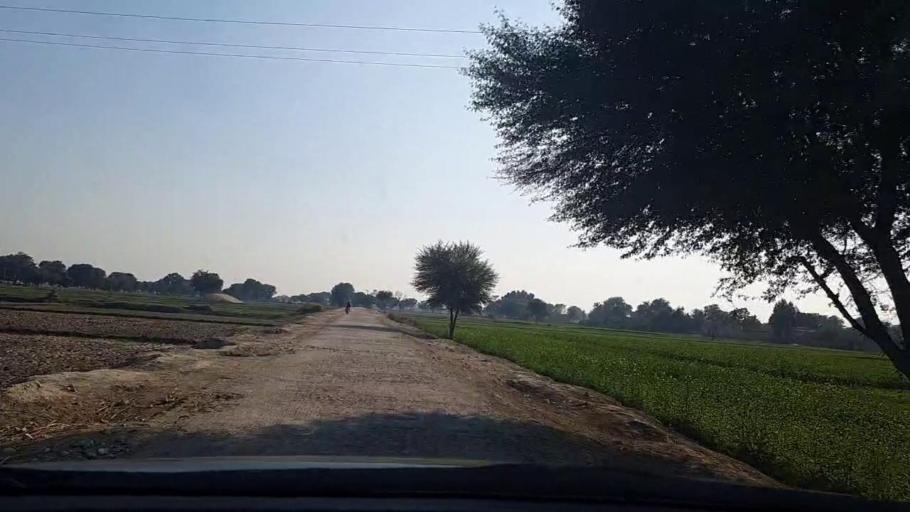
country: PK
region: Sindh
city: Sehwan
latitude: 26.3231
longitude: 68.0063
